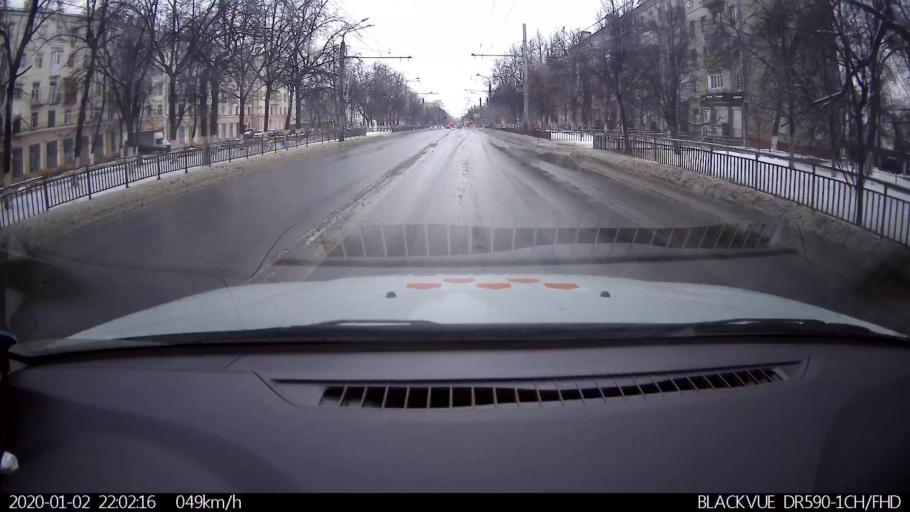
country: RU
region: Nizjnij Novgorod
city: Gorbatovka
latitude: 56.2465
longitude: 43.8646
